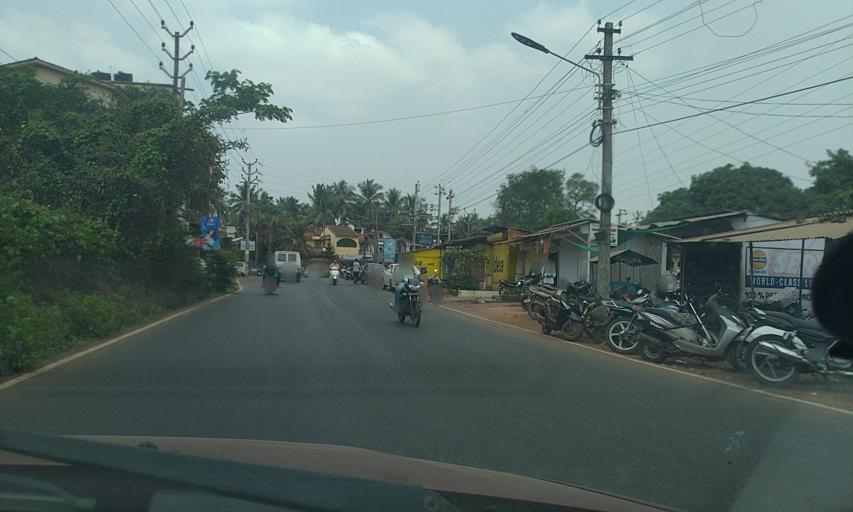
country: IN
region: Goa
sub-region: North Goa
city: Mapuca
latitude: 15.6024
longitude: 73.8054
